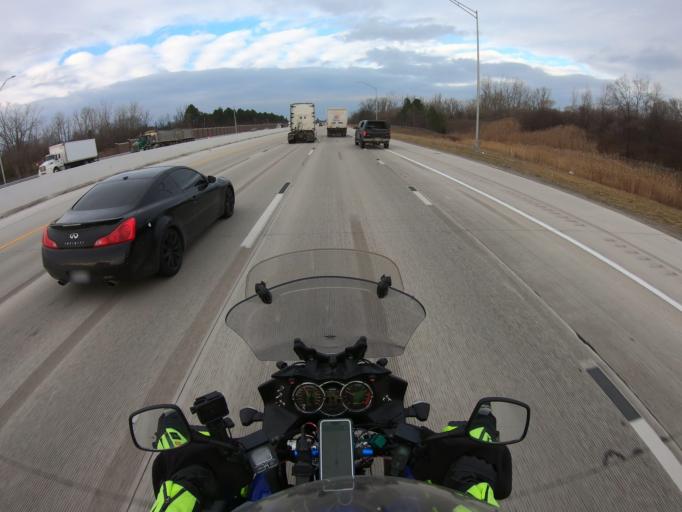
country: US
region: Michigan
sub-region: Oakland County
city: Troy
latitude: 42.5711
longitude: -83.1545
